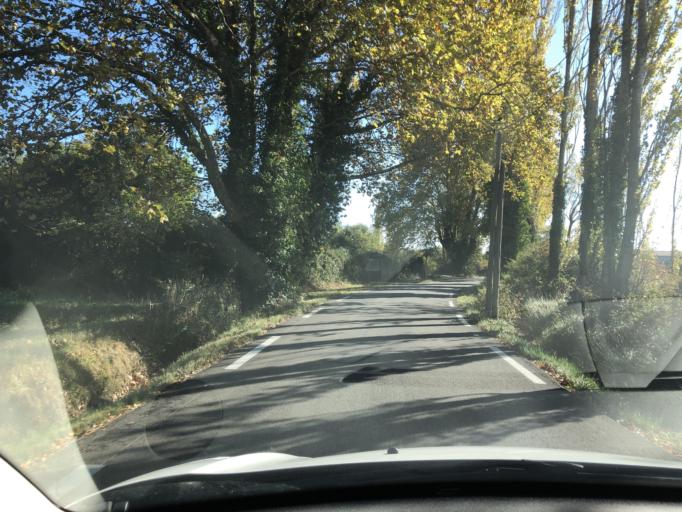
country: FR
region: Provence-Alpes-Cote d'Azur
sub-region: Departement du Vaucluse
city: Entraigues-sur-la-Sorgue
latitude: 43.9867
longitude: 4.9381
